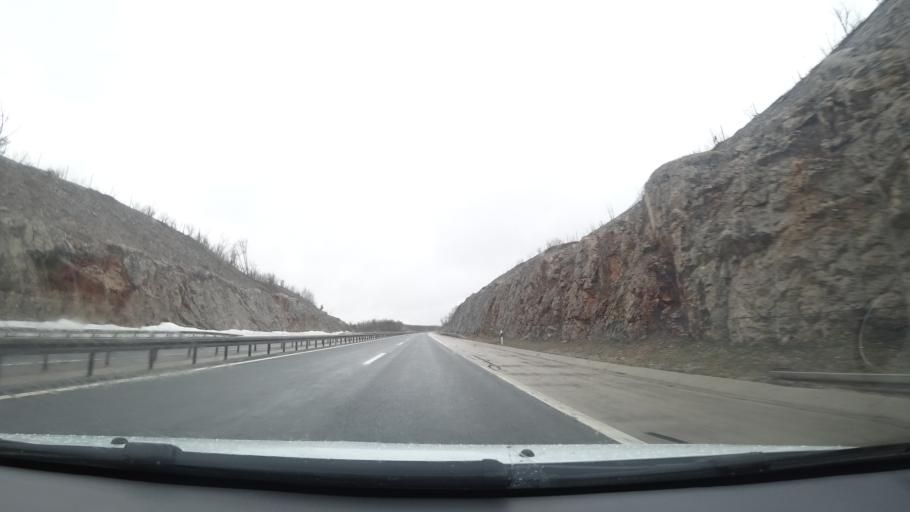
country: HR
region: Licko-Senjska
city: Gospic
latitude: 44.6999
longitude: 15.3962
